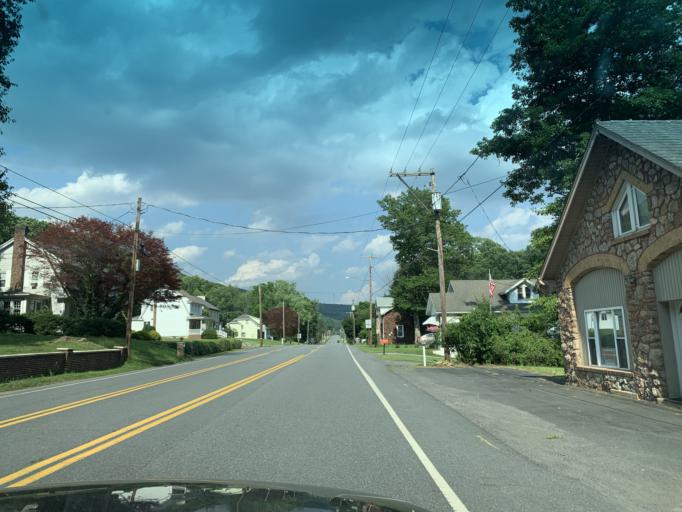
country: US
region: Pennsylvania
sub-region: Schuylkill County
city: Ashland
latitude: 40.7739
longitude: -76.3152
